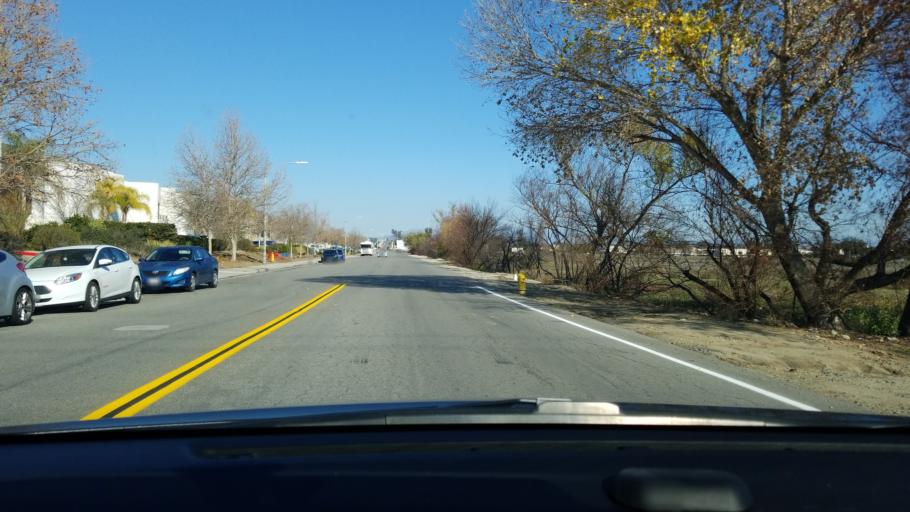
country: US
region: California
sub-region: Riverside County
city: Murrieta Hot Springs
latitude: 33.5243
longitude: -117.1759
